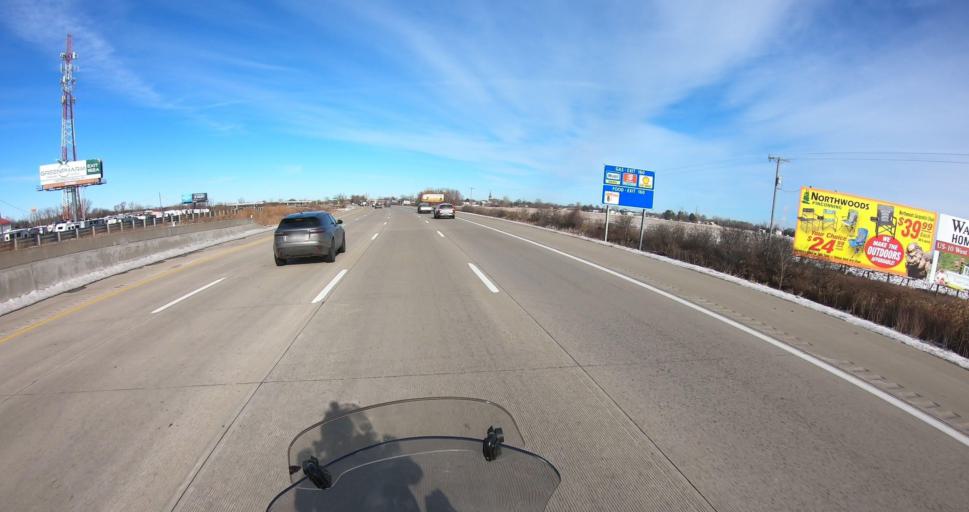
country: US
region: Michigan
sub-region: Bay County
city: Bay City
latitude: 43.5530
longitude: -83.9443
